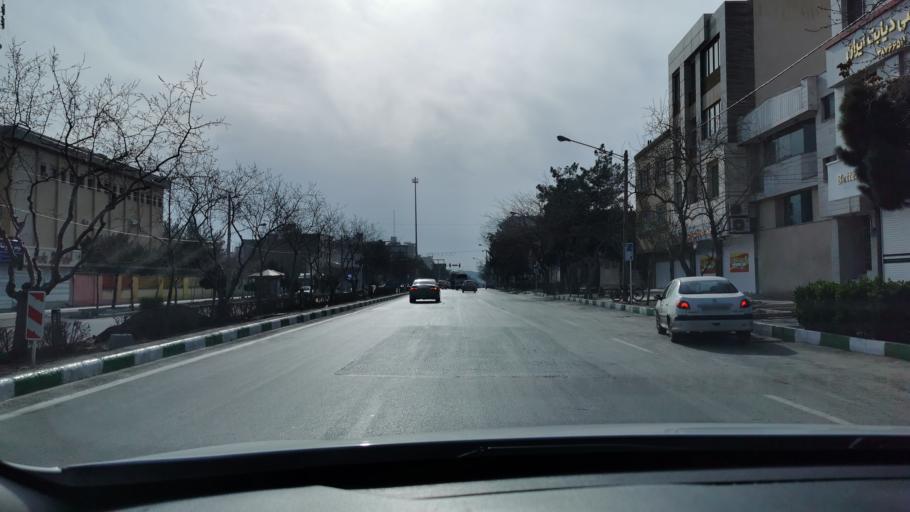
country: IR
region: Razavi Khorasan
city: Mashhad
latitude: 36.2918
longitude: 59.5363
